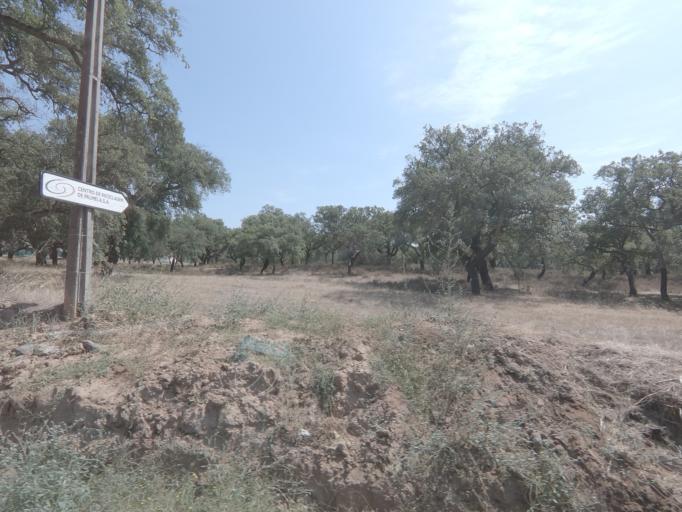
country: PT
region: Setubal
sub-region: Palmela
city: Palmela
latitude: 38.5886
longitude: -8.8519
